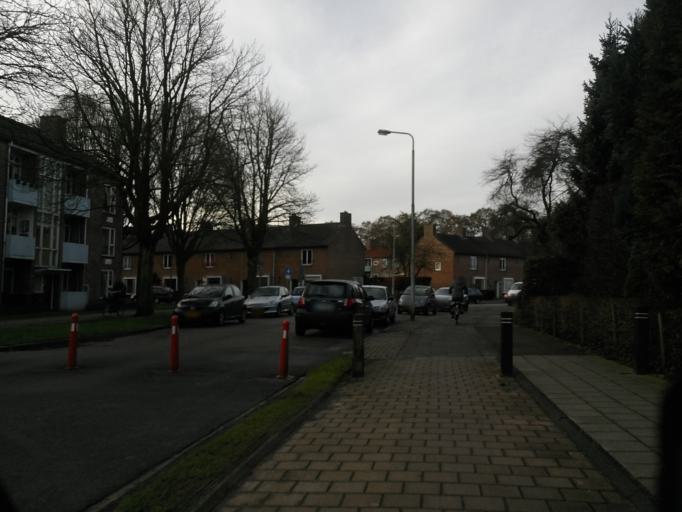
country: NL
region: Utrecht
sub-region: Gemeente Amersfoort
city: Randenbroek
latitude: 52.1519
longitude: 5.4047
